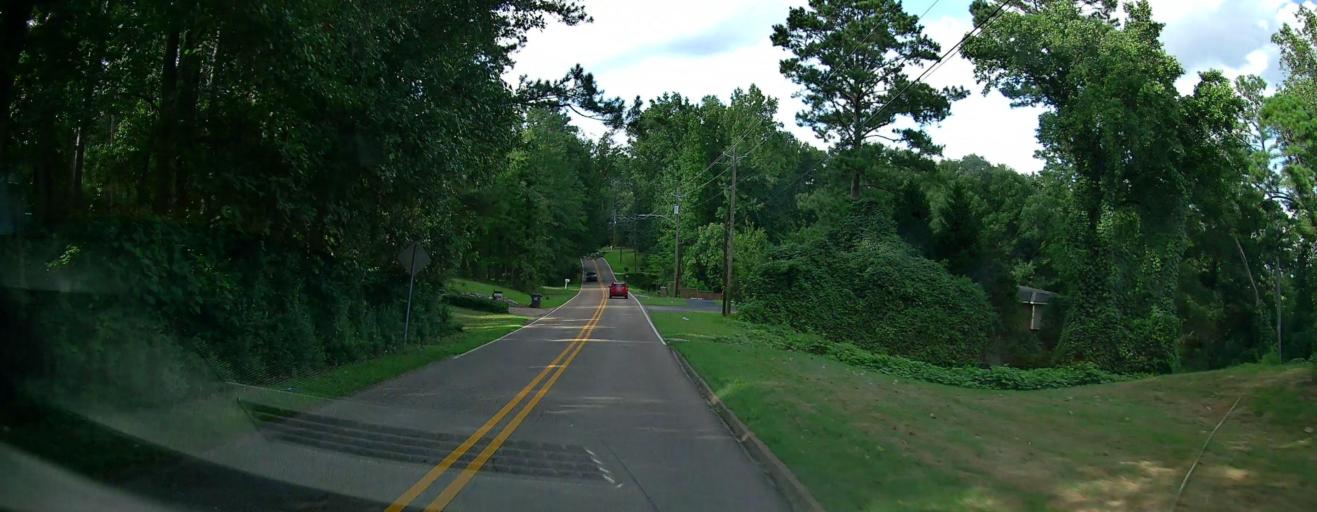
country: US
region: Alabama
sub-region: Russell County
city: Phenix City
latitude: 32.4935
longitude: -85.0001
